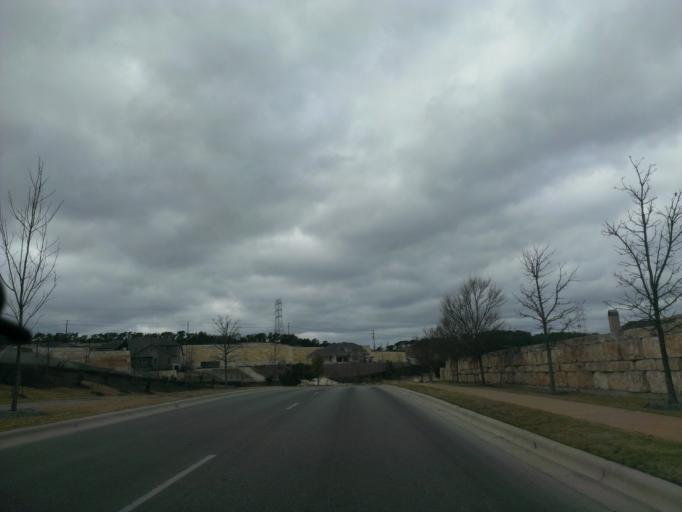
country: US
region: Texas
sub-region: Travis County
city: The Hills
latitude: 30.3500
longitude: -98.0124
